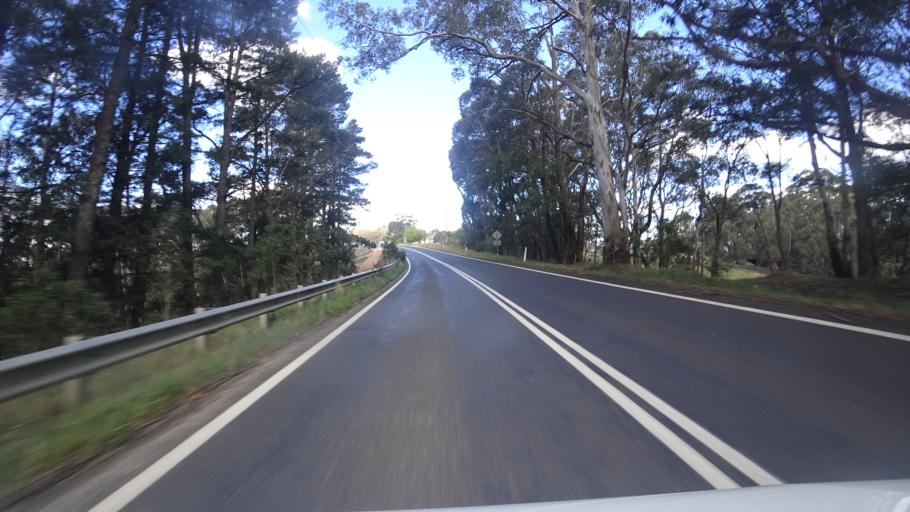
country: AU
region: New South Wales
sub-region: Lithgow
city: Bowenfels
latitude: -33.6392
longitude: 150.0557
